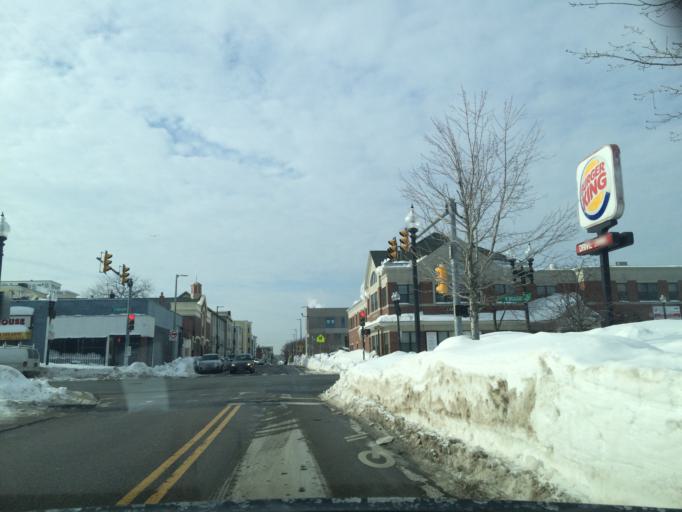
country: US
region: Massachusetts
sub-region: Suffolk County
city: South Boston
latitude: 42.3391
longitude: -71.0505
